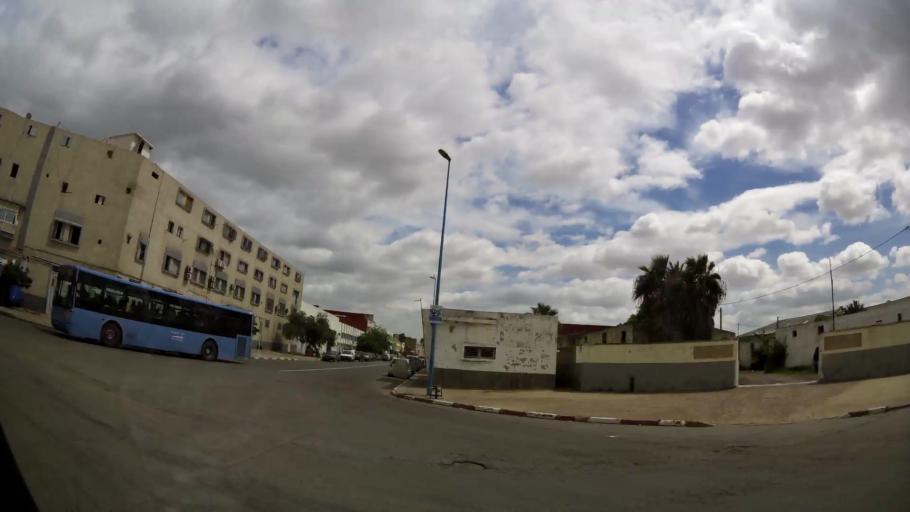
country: MA
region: Grand Casablanca
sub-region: Casablanca
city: Casablanca
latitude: 33.6055
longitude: -7.5630
